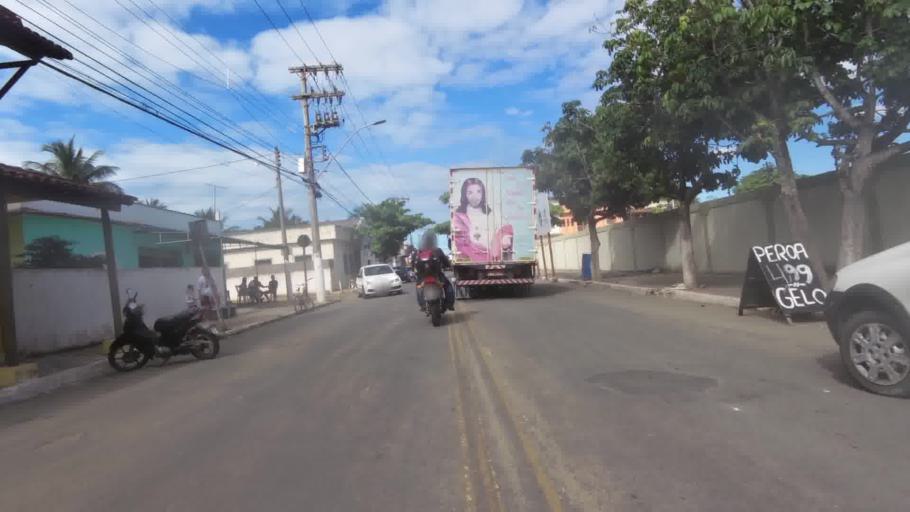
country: BR
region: Espirito Santo
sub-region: Itapemirim
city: Itapemirim
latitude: -21.0078
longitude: -40.8083
